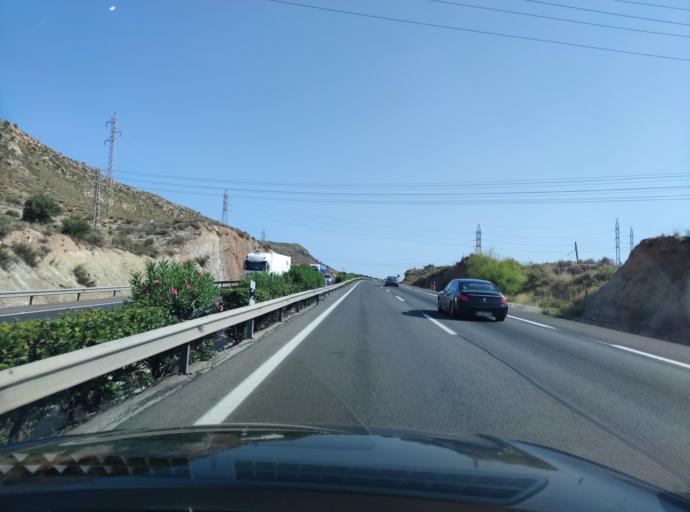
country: ES
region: Valencia
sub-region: Provincia de Alicante
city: Elda
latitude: 38.4382
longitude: -0.7832
